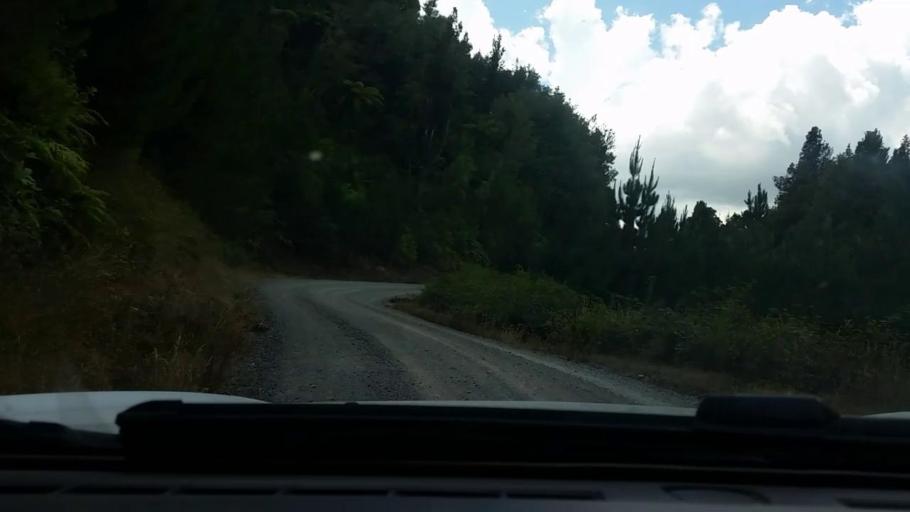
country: NZ
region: Bay of Plenty
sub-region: Kawerau District
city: Kawerau
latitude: -38.0304
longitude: 176.5558
